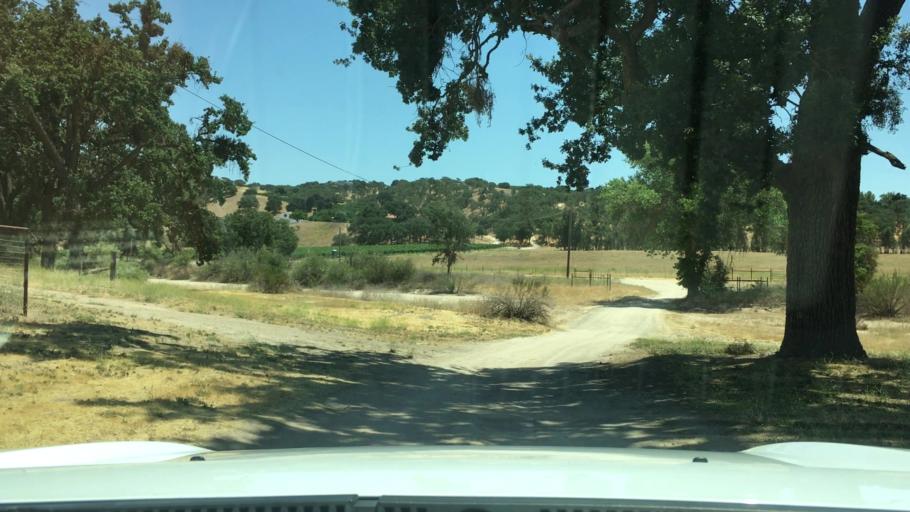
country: US
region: California
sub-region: San Luis Obispo County
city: Paso Robles
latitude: 35.5964
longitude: -120.6034
